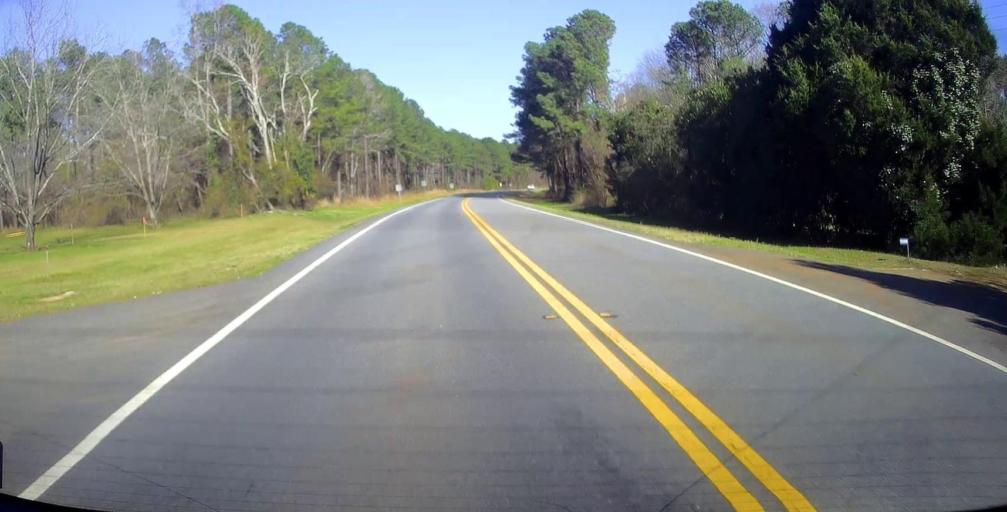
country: US
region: Georgia
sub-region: Dooly County
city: Unadilla
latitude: 32.3375
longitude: -83.8524
